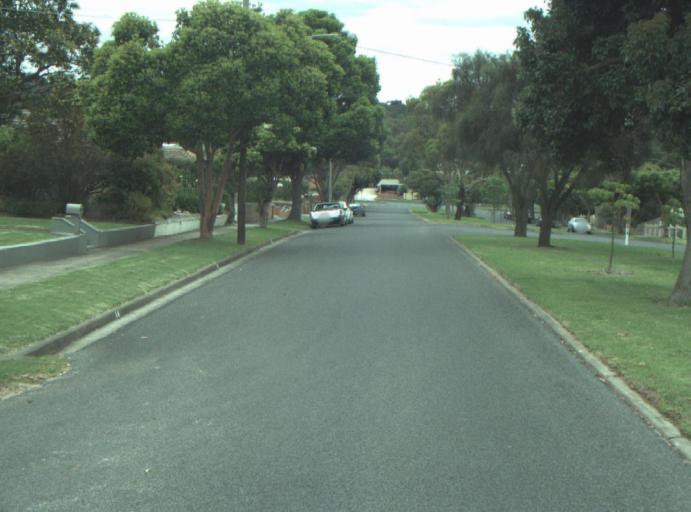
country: AU
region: Victoria
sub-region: Greater Geelong
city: East Geelong
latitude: -38.1572
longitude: 144.3815
